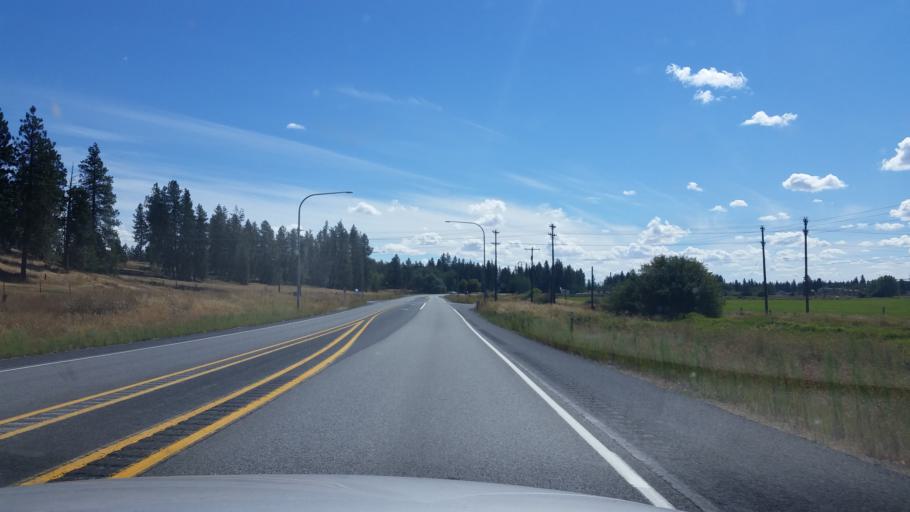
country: US
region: Washington
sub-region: Spokane County
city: Cheney
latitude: 47.5303
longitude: -117.5702
